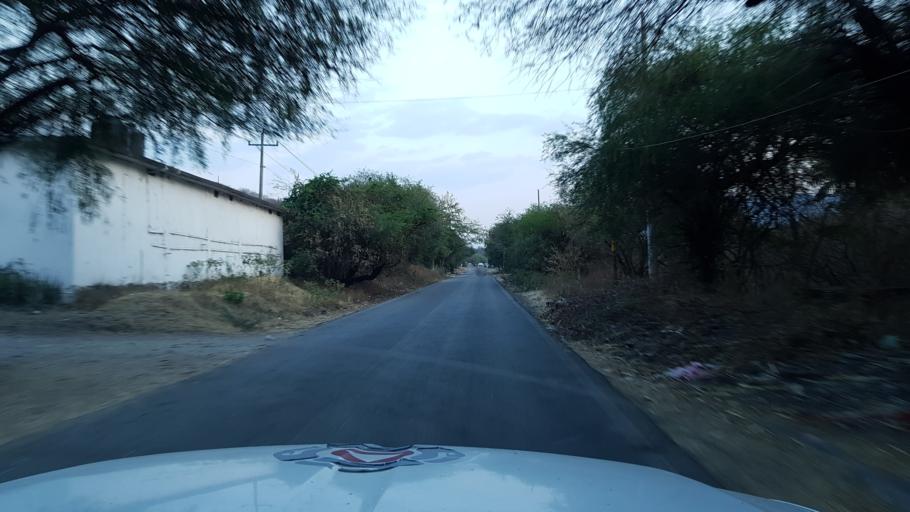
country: MX
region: Morelos
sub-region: Tlaltizapan de Zapata
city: Colonia Palo Prieto (Chipitongo)
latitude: 18.7089
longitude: -99.1073
